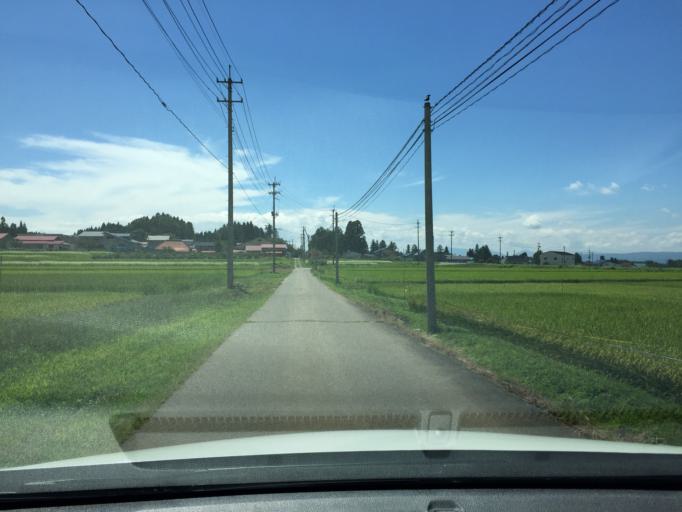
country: JP
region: Fukushima
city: Inawashiro
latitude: 37.5690
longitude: 140.1363
